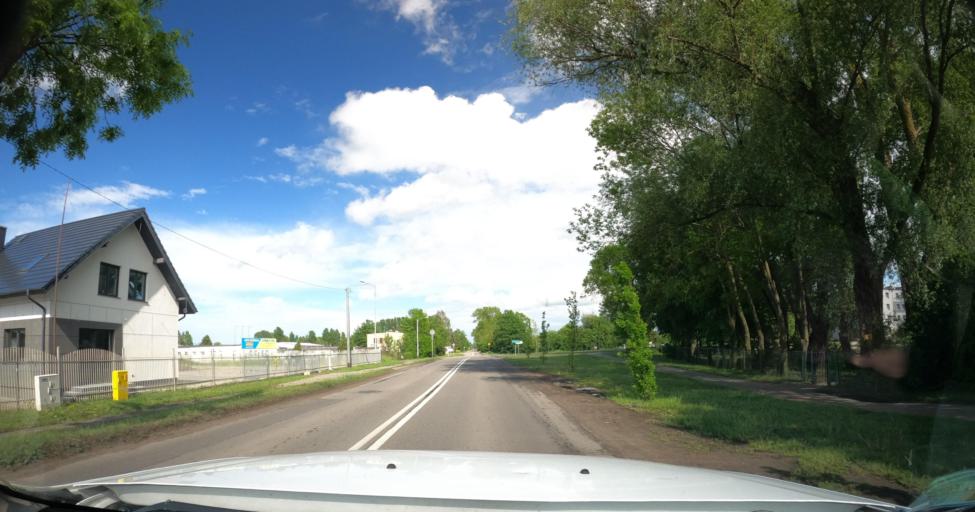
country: PL
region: Pomeranian Voivodeship
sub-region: Powiat nowodworski
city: Nowy Dwor Gdanski
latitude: 54.2090
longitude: 19.1336
